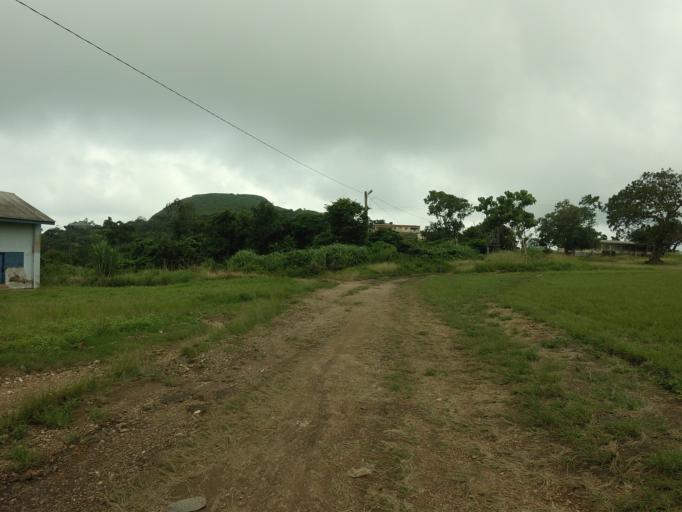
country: GH
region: Volta
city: Kpandu
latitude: 6.8506
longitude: 0.4349
